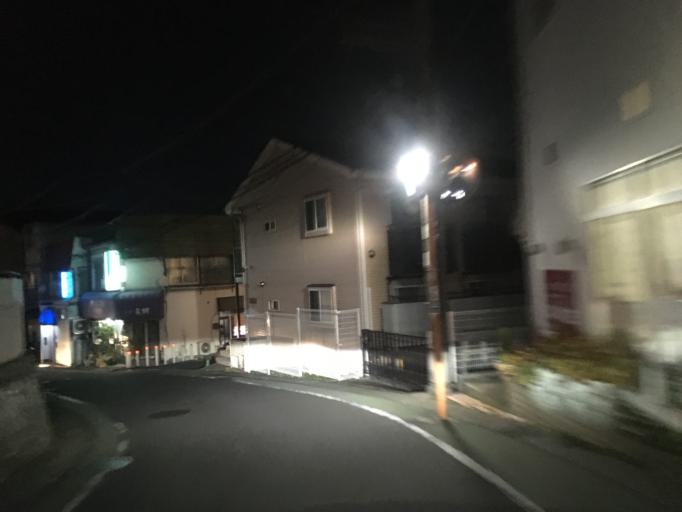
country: JP
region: Tokyo
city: Chofugaoka
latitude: 35.6096
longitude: 139.5200
